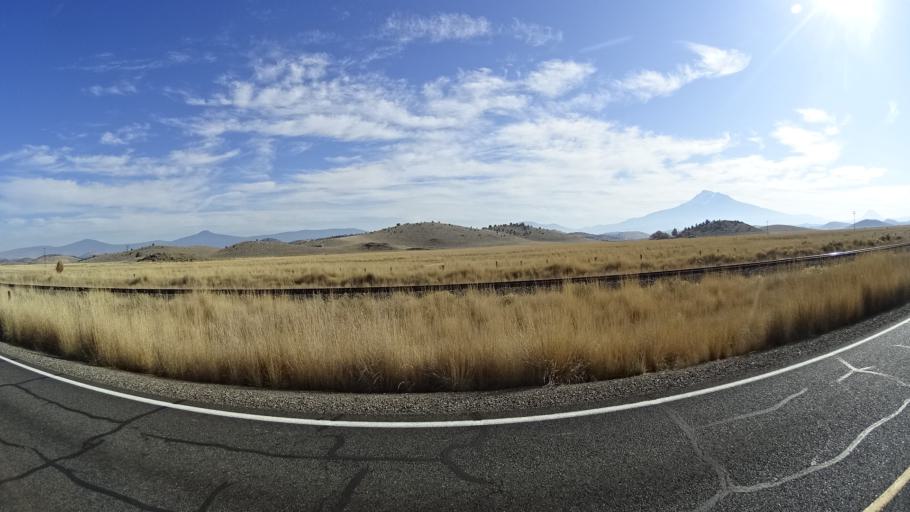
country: US
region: California
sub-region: Siskiyou County
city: Montague
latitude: 41.5863
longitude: -122.5245
